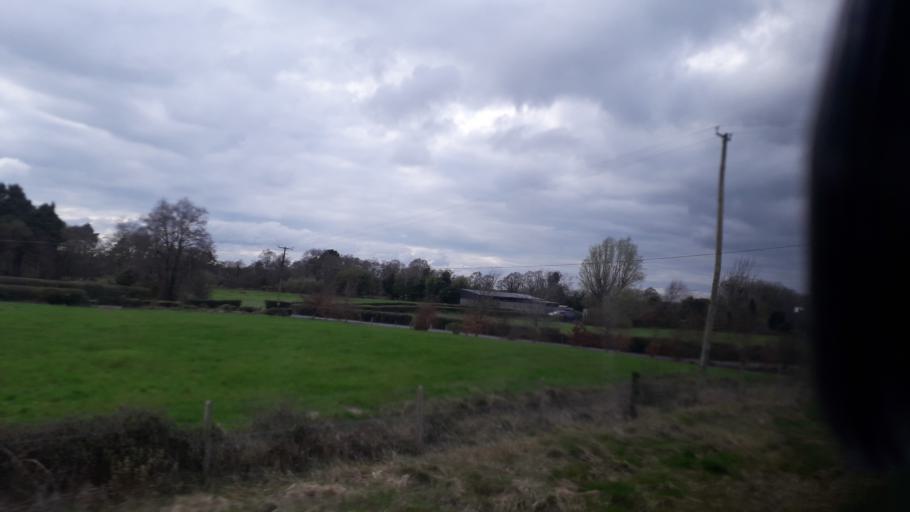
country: IE
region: Leinster
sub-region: An Iarmhi
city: Castlepollard
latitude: 53.6458
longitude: -7.4237
